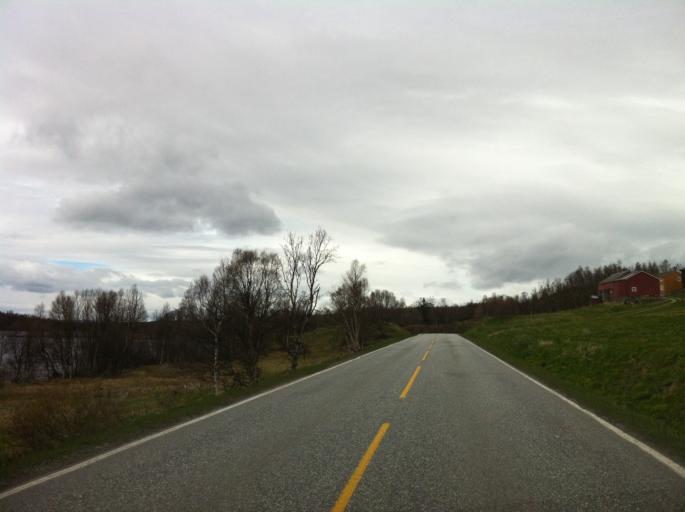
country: NO
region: Sor-Trondelag
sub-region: Roros
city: Roros
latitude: 62.5991
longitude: 11.5107
